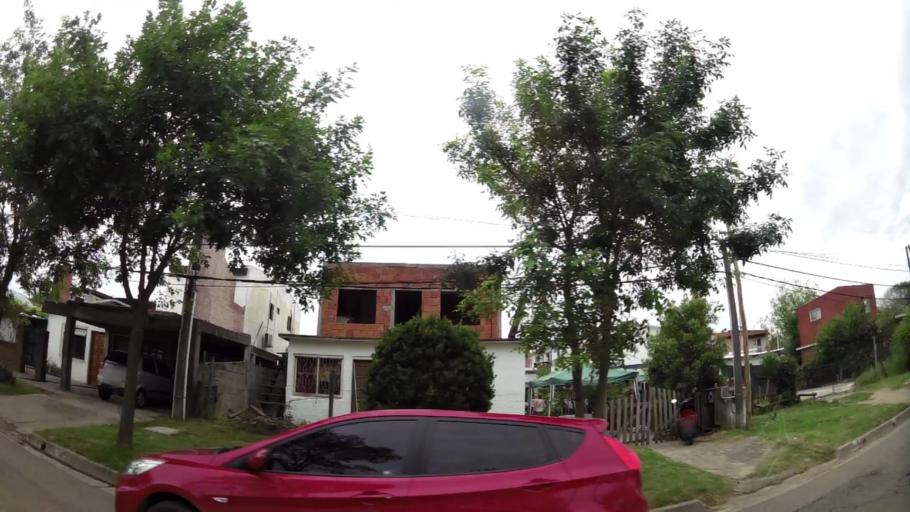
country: UY
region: Maldonado
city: Maldonado
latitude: -34.8902
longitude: -54.9502
